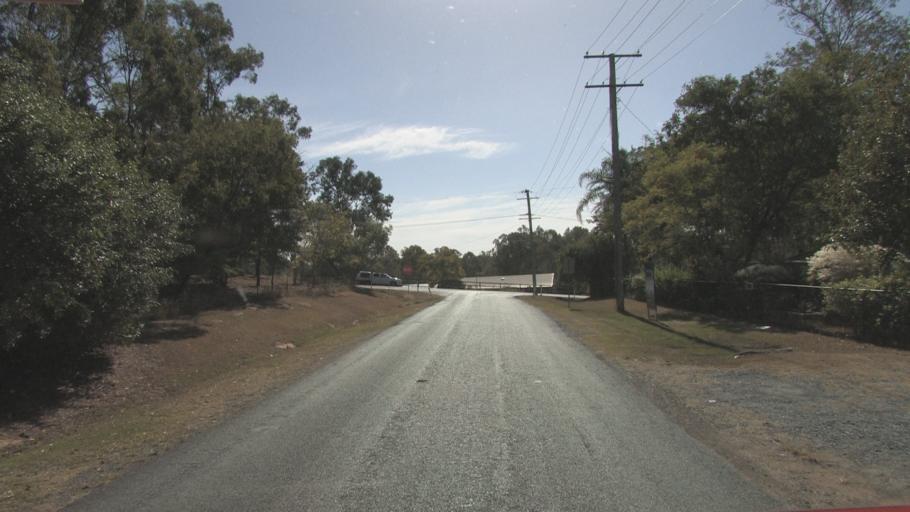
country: AU
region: Queensland
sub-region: Logan
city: Cedar Vale
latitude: -27.8508
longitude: 152.9917
